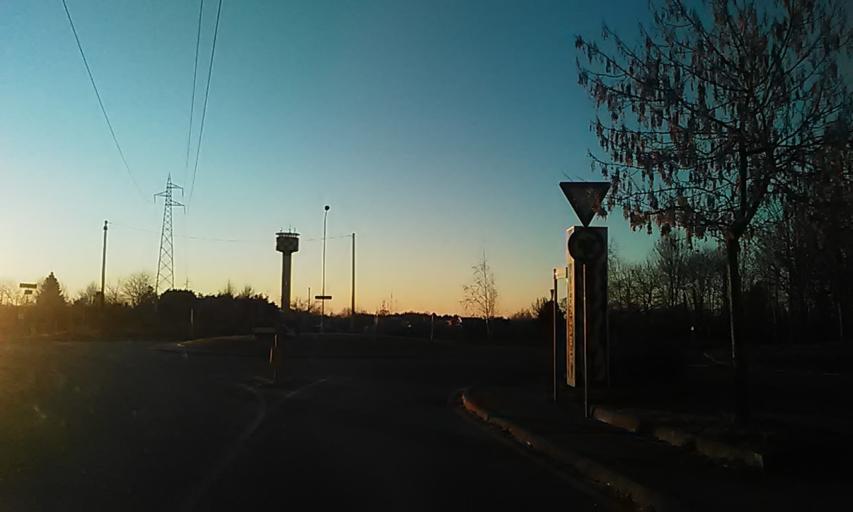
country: IT
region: Piedmont
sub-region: Provincia di Biella
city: Gaglianico
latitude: 45.5479
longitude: 8.0824
